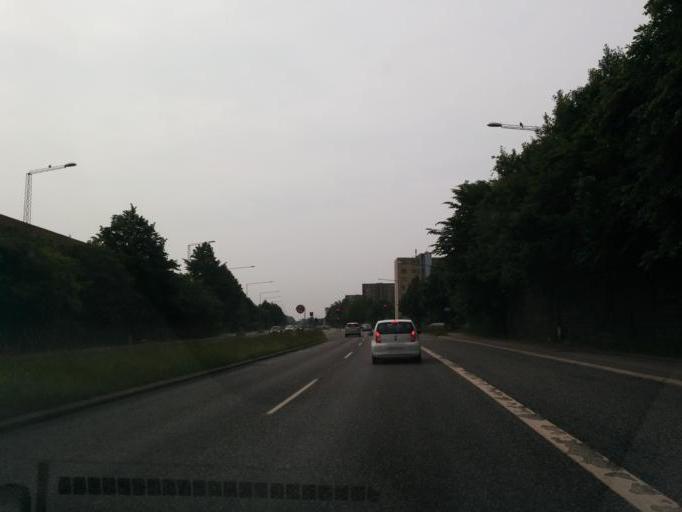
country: DK
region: Central Jutland
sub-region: Arhus Kommune
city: Arhus
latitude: 56.1937
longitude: 10.2189
